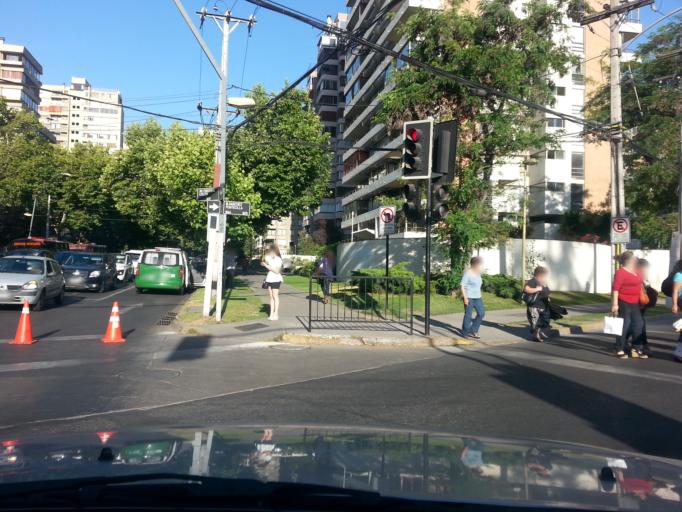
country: CL
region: Santiago Metropolitan
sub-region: Provincia de Santiago
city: Villa Presidente Frei, Nunoa, Santiago, Chile
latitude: -33.4261
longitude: -70.5906
